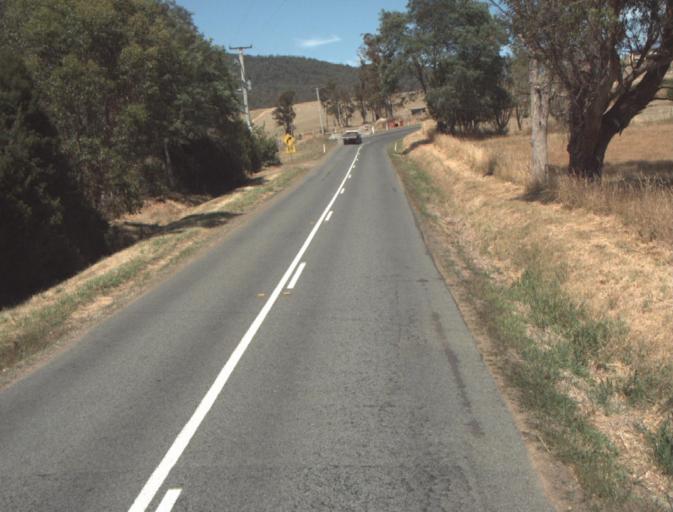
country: AU
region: Tasmania
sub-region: Launceston
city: Mayfield
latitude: -41.2571
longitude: 147.1462
